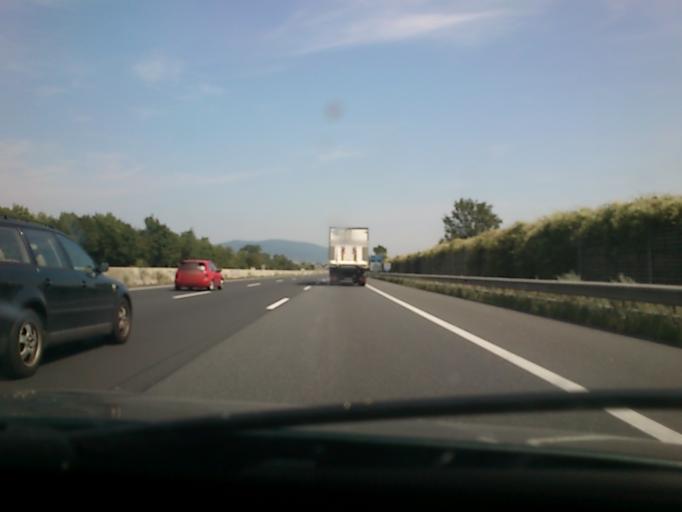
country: AT
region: Lower Austria
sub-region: Politischer Bezirk Baden
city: Leobersdorf
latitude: 47.9420
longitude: 16.2133
